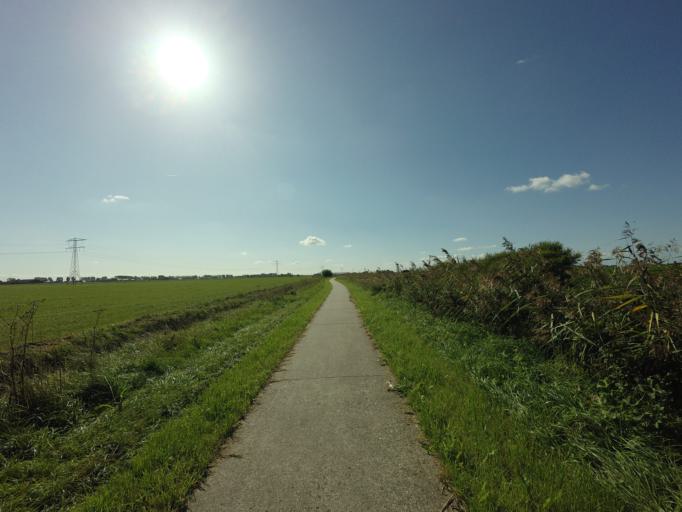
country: NL
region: Friesland
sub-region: Gemeente Boarnsterhim
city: Reduzum
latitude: 53.1456
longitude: 5.7642
